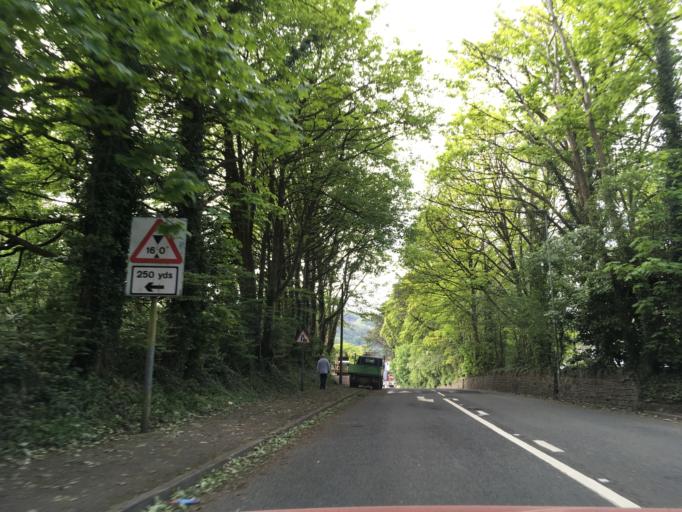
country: GB
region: Wales
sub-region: Cardiff
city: Radyr
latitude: 51.5302
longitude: -3.2471
